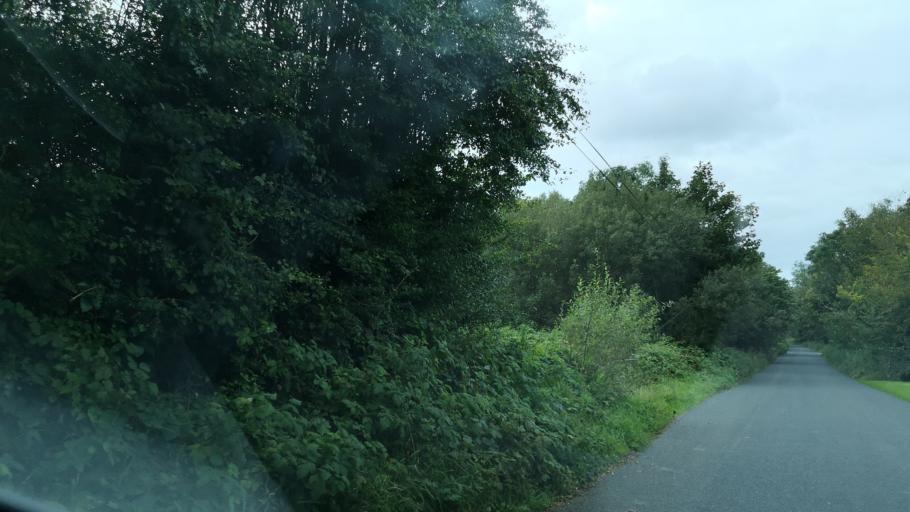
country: IE
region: Connaught
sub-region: County Galway
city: Loughrea
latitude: 53.1545
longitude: -8.4389
